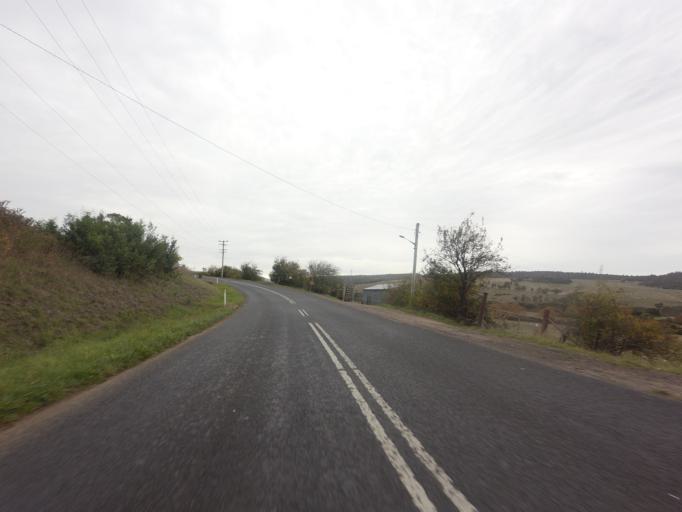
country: AU
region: Tasmania
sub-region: Derwent Valley
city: New Norfolk
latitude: -42.6050
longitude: 147.0771
